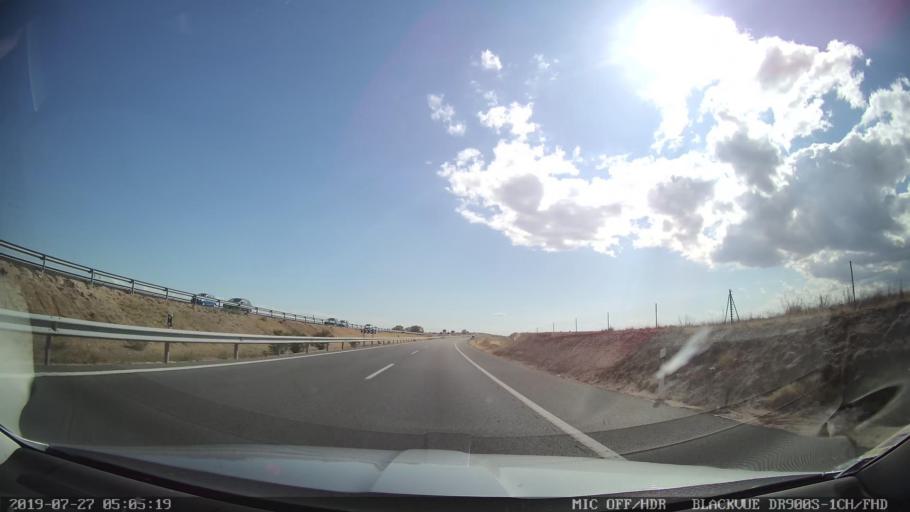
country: ES
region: Castille-La Mancha
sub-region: Province of Toledo
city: La Torre de Esteban Hambran
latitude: 40.1423
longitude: -4.1902
